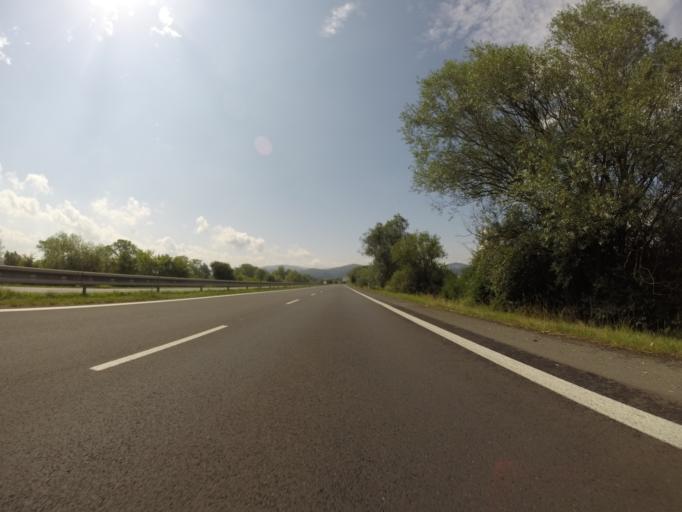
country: SK
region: Banskobystricky
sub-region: Okres Banska Bystrica
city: Zvolen
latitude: 48.5941
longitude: 19.1098
